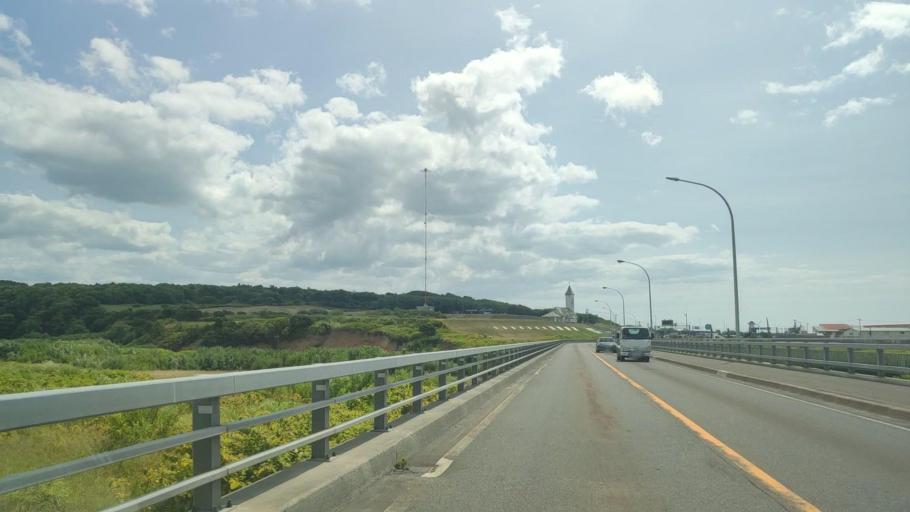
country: JP
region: Hokkaido
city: Makubetsu
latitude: 44.7182
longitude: 141.7933
